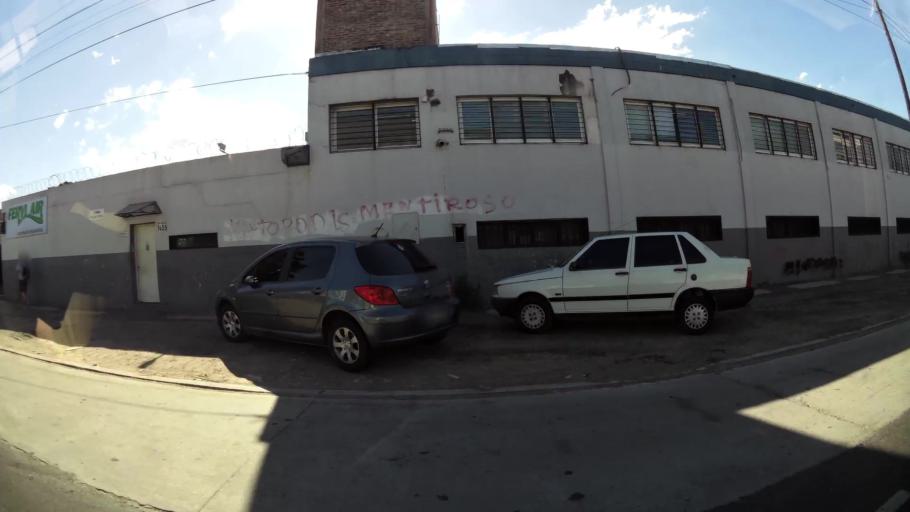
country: AR
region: Buenos Aires
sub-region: Partido de General San Martin
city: General San Martin
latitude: -34.5203
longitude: -58.5700
